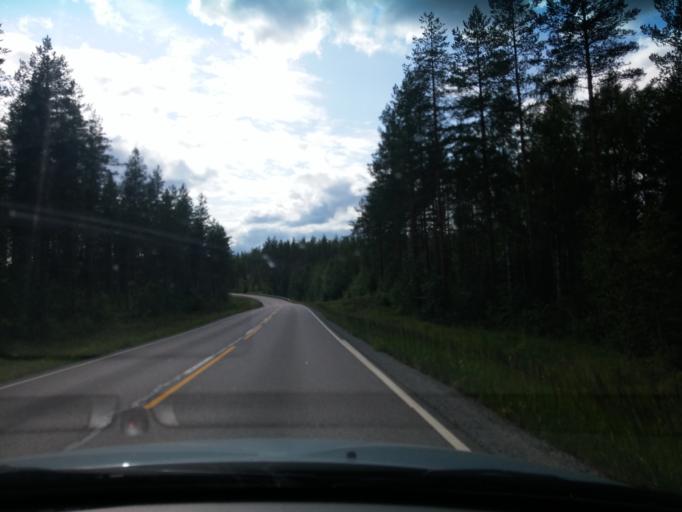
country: FI
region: Central Finland
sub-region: Saarijaervi-Viitasaari
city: Pylkoenmaeki
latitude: 62.5938
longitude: 24.6044
